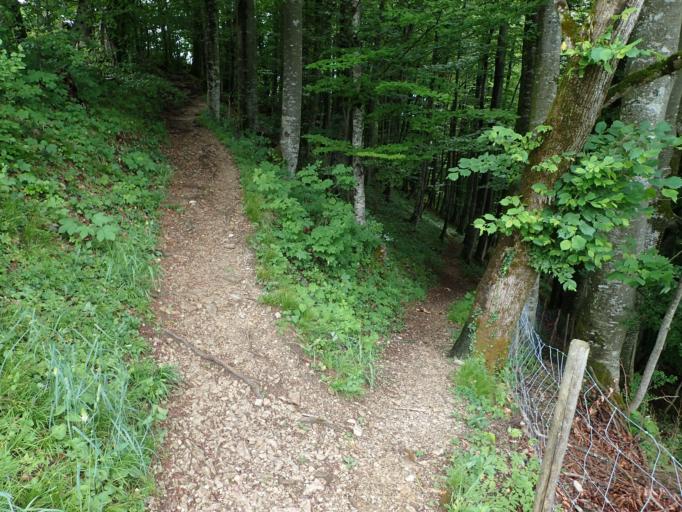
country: AT
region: Upper Austria
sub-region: Politischer Bezirk Gmunden
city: Sankt Wolfgang im Salzkammergut
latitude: 47.7429
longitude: 13.4441
